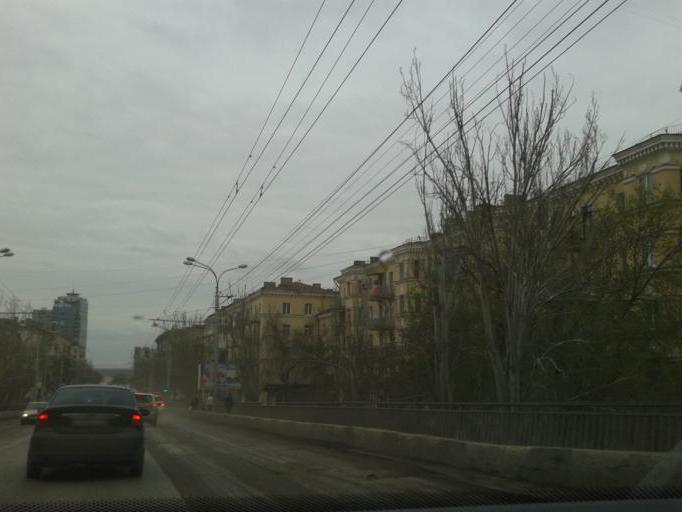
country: RU
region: Volgograd
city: Volgograd
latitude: 48.7120
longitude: 44.5164
